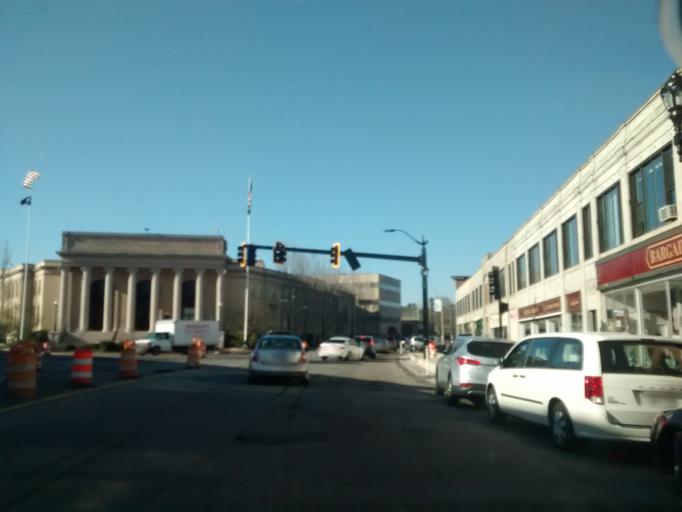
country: US
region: Massachusetts
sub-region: Middlesex County
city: Framingham
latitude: 42.2788
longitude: -71.4167
